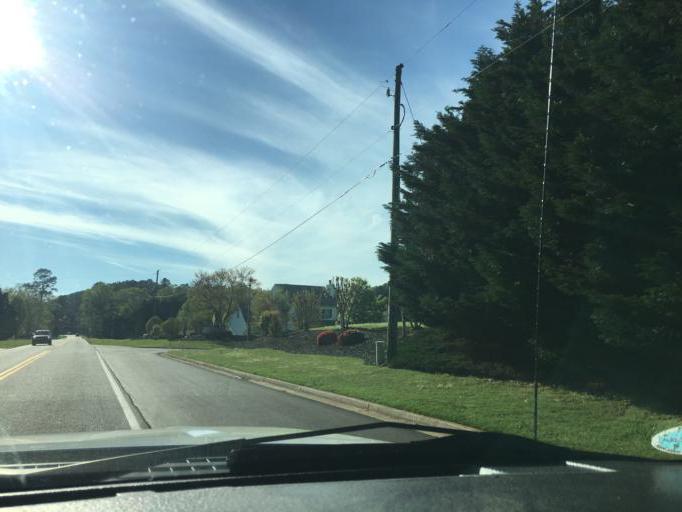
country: US
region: Georgia
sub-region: Dawson County
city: Dawsonville
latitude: 34.3326
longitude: -84.0973
